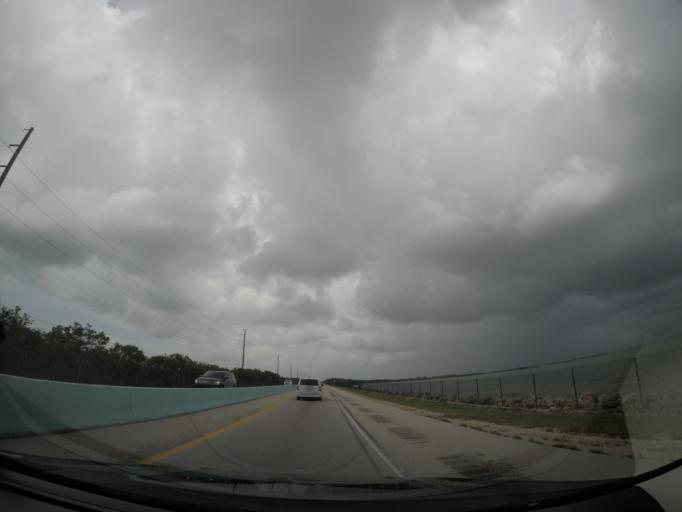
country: US
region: Florida
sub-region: Monroe County
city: North Key Largo
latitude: 25.2028
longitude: -80.4197
